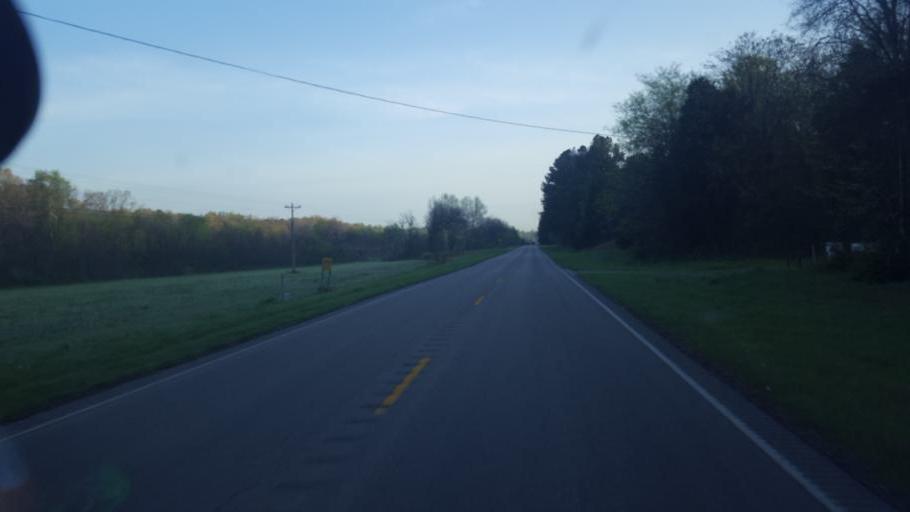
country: US
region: Kentucky
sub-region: Hart County
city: Munfordville
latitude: 37.3379
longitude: -85.9092
